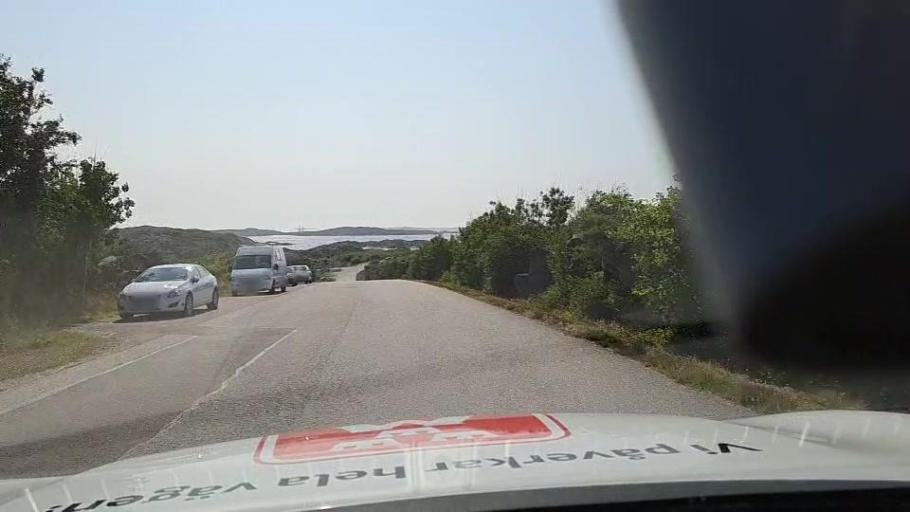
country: SE
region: Vaestra Goetaland
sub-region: Lysekils Kommun
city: Lysekil
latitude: 58.1193
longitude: 11.4606
